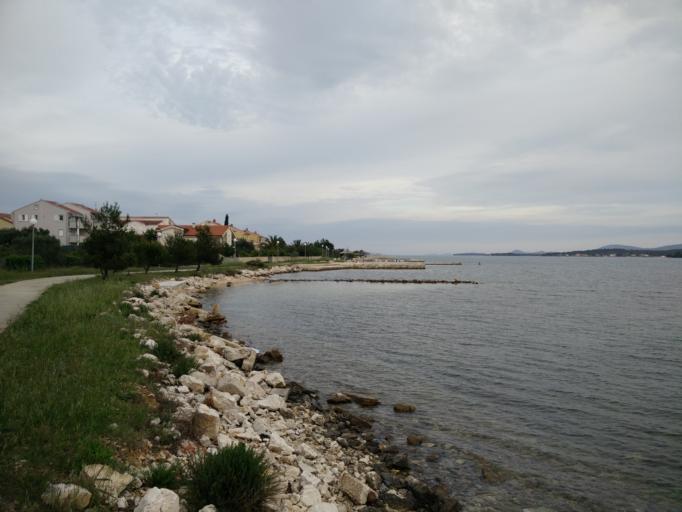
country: HR
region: Zadarska
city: Turanj
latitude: 43.9778
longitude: 15.3943
